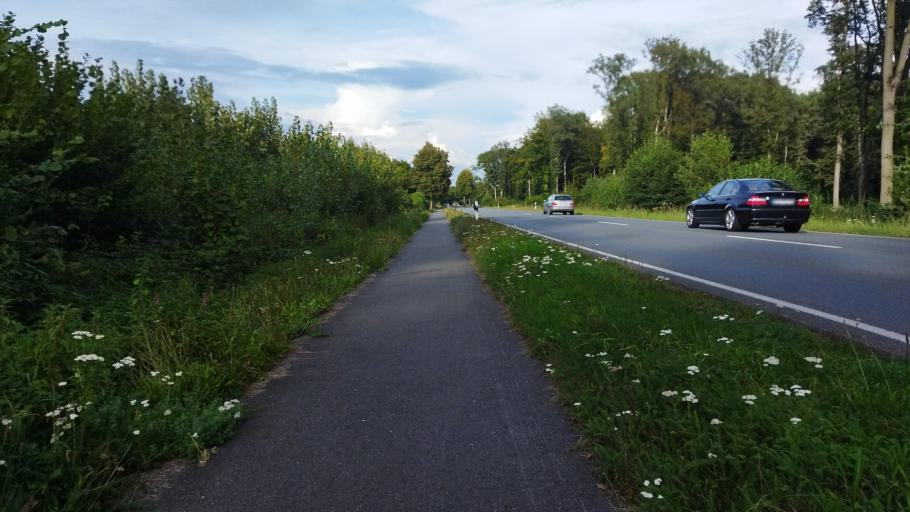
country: DE
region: North Rhine-Westphalia
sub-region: Regierungsbezirk Munster
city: Ostbevern
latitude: 52.0566
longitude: 7.9305
